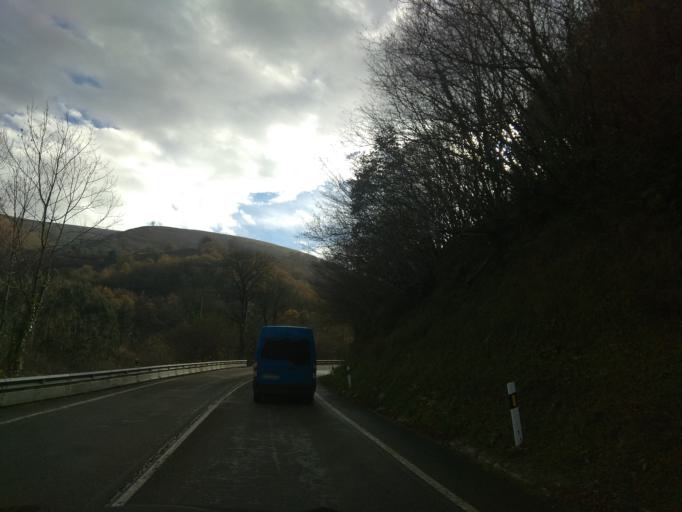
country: ES
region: Cantabria
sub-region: Provincia de Cantabria
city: San Pedro del Romeral
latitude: 43.1452
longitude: -3.8995
